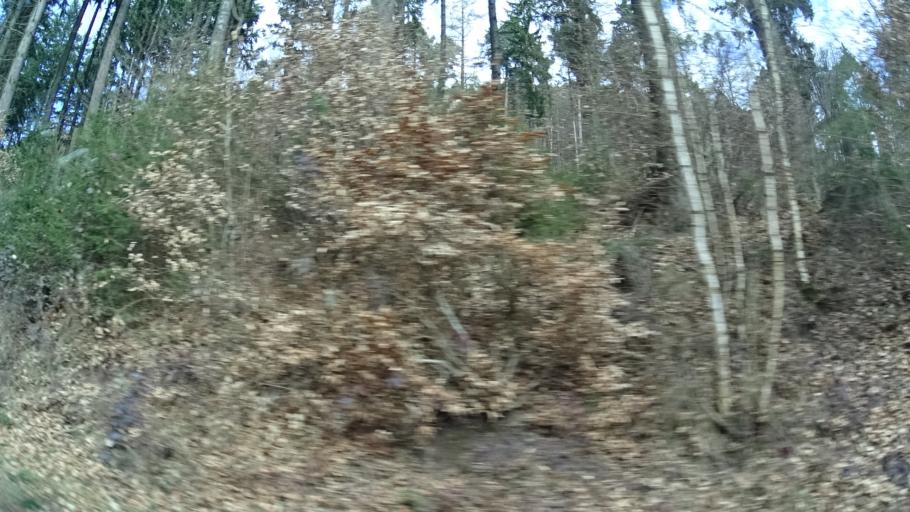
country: DE
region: Rheinland-Pfalz
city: Sankt Martin
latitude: 49.2955
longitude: 8.0509
